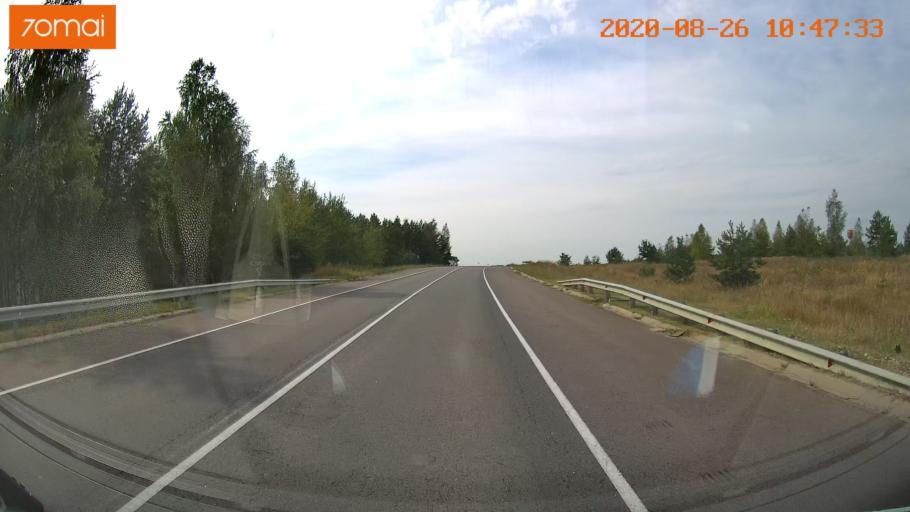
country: RU
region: Rjazan
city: Lashma
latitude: 54.7255
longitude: 41.1883
